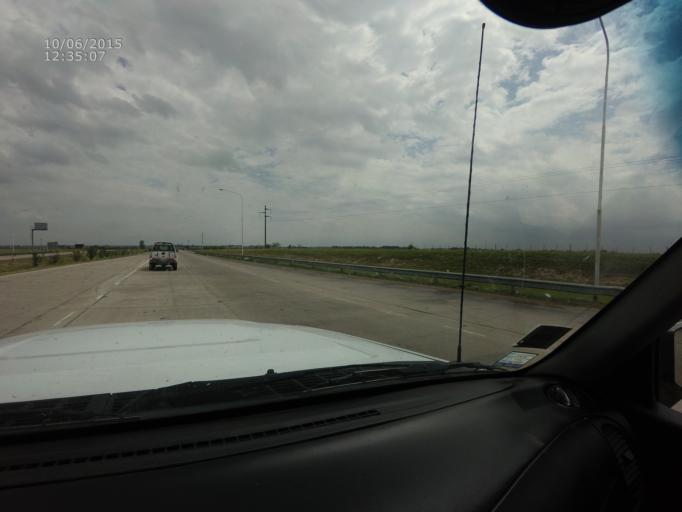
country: AR
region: Santa Fe
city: Carcarana
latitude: -32.8759
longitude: -61.1722
